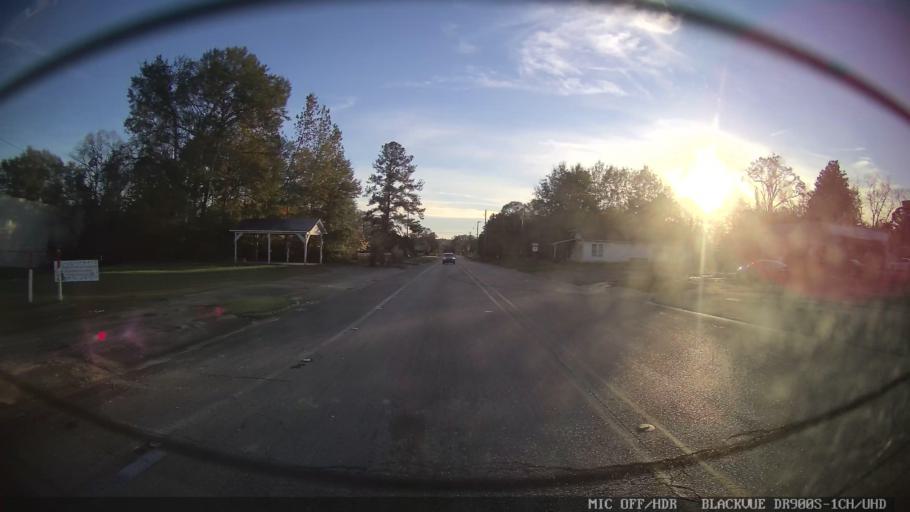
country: US
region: Mississippi
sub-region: Lamar County
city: Lumberton
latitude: 31.0014
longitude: -89.4525
